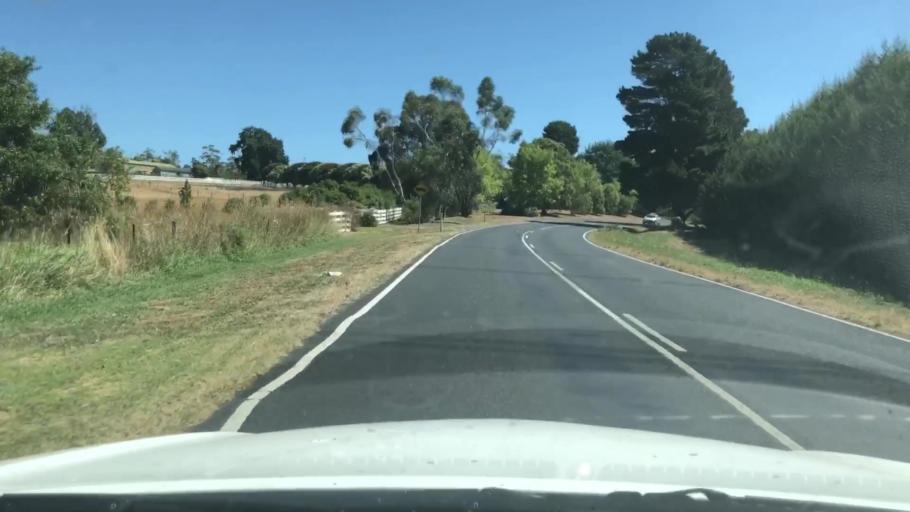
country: AU
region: Victoria
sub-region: Yarra Ranges
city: Woori Yallock
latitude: -37.8053
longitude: 145.5229
